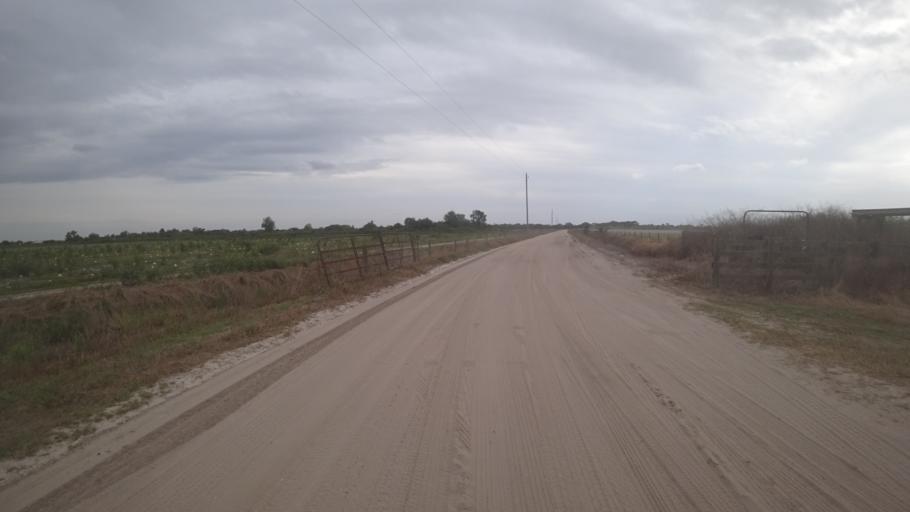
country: US
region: Florida
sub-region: Sarasota County
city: Warm Mineral Springs
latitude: 27.2794
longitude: -82.1700
